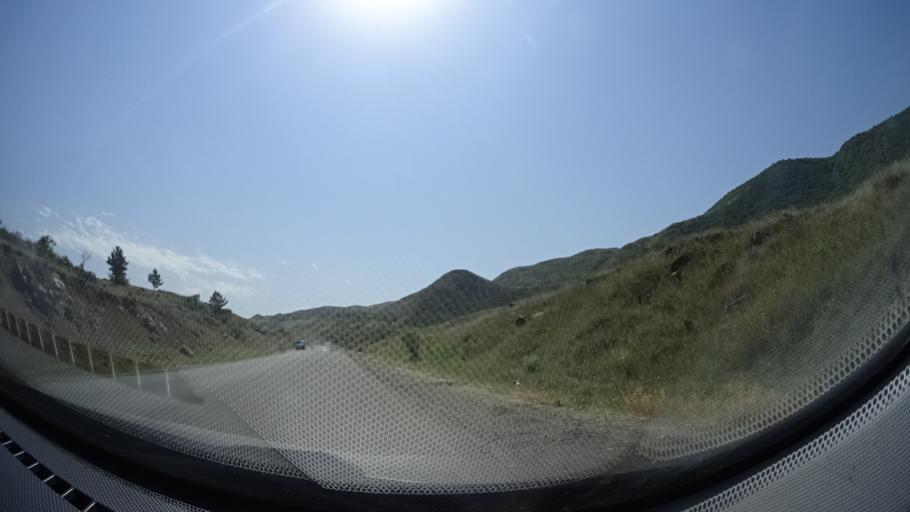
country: GE
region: Samtskhe-Javakheti
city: Aspindza
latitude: 41.5929
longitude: 43.1716
